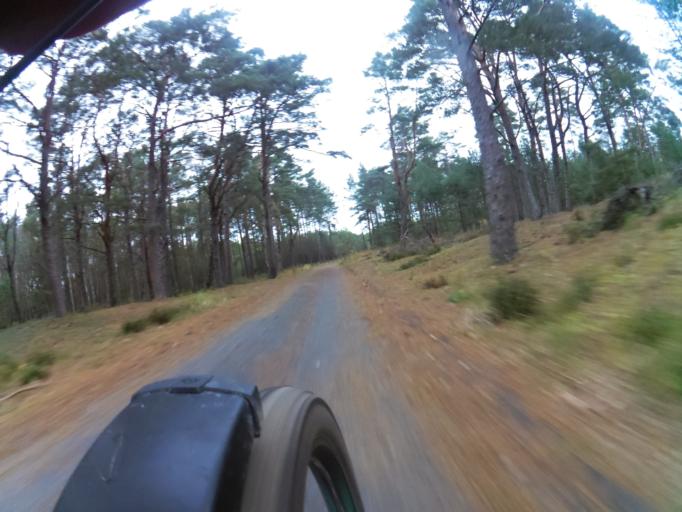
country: PL
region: Pomeranian Voivodeship
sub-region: Powiat wejherowski
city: Choczewo
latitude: 54.7859
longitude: 17.7468
